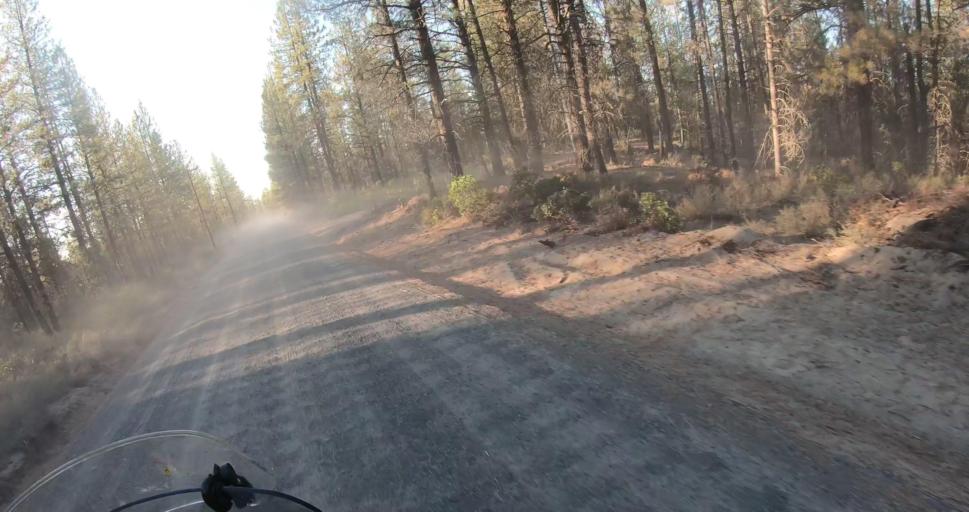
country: US
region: Oregon
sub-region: Deschutes County
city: La Pine
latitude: 43.7166
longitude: -121.3891
